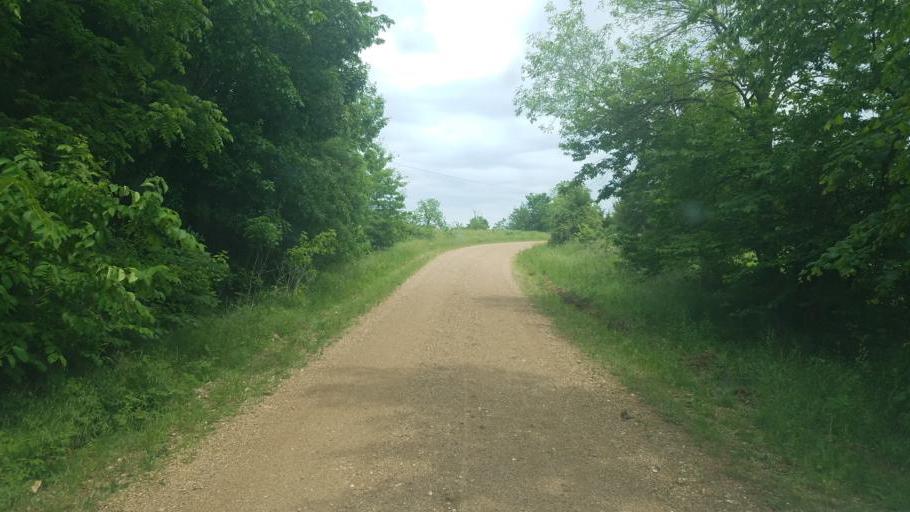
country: US
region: Missouri
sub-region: Moniteau County
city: Tipton
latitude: 38.5511
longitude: -92.7431
